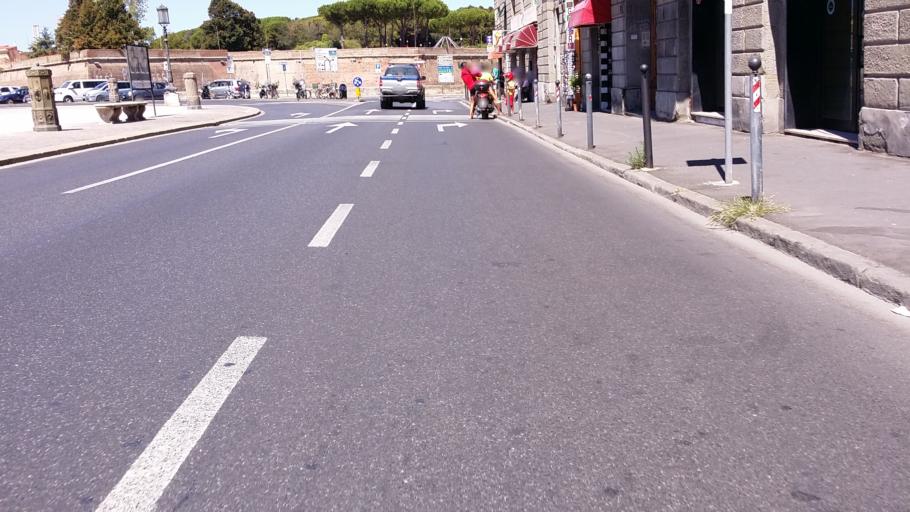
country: IT
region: Tuscany
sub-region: Provincia di Livorno
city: Livorno
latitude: 43.5530
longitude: 10.3142
